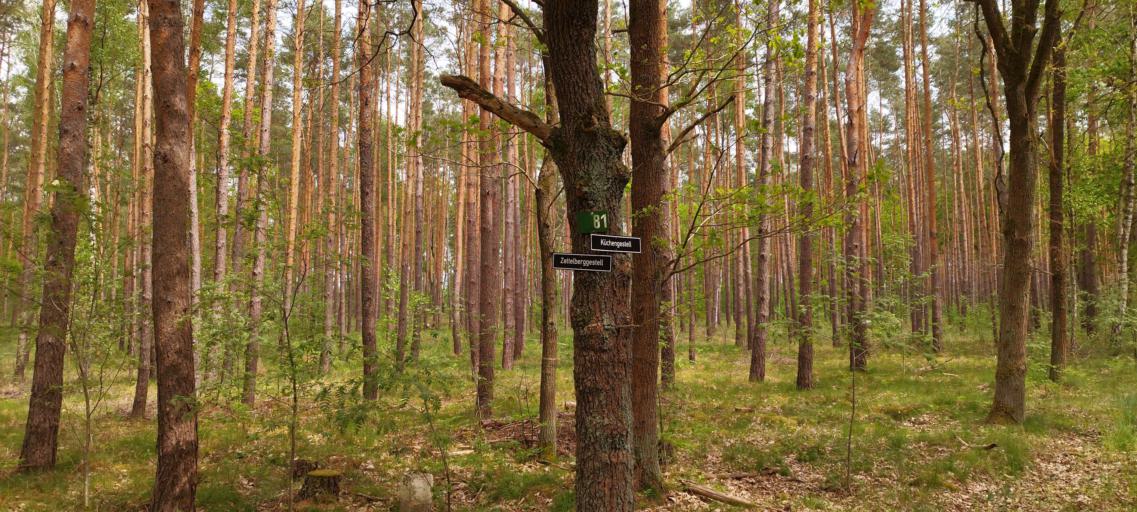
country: DE
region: Brandenburg
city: Spreenhagen
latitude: 52.3842
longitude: 13.9330
